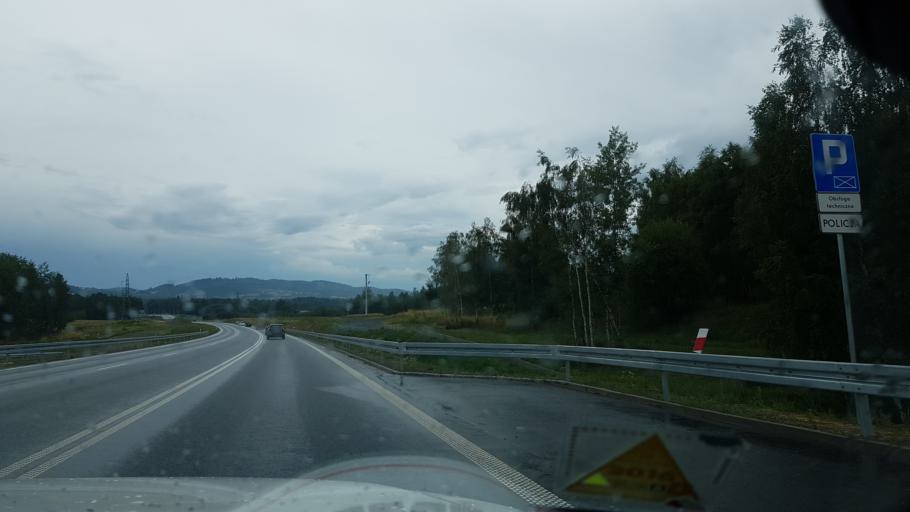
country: PL
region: Lower Silesian Voivodeship
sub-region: Powiat jeleniogorski
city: Myslakowice
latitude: 50.9000
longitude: 15.8399
